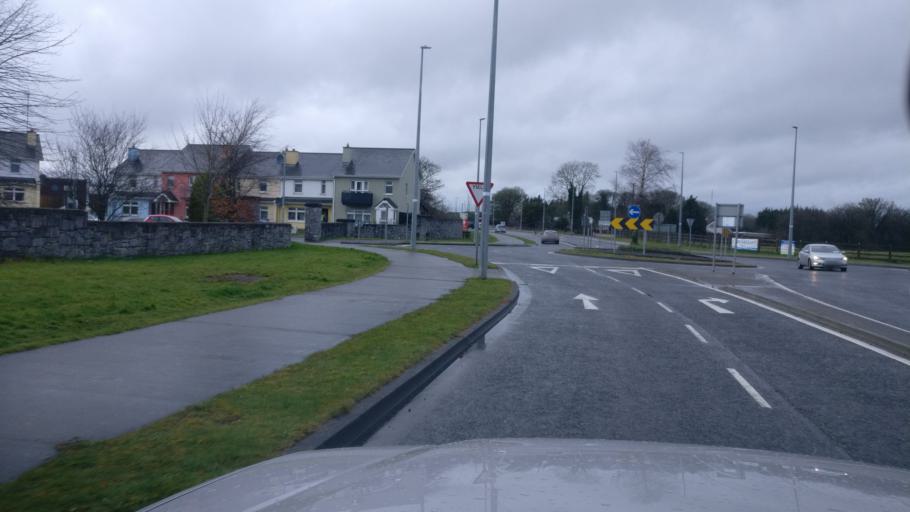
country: IE
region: Leinster
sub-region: An Iarmhi
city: Athlone
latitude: 53.4234
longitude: -7.9977
